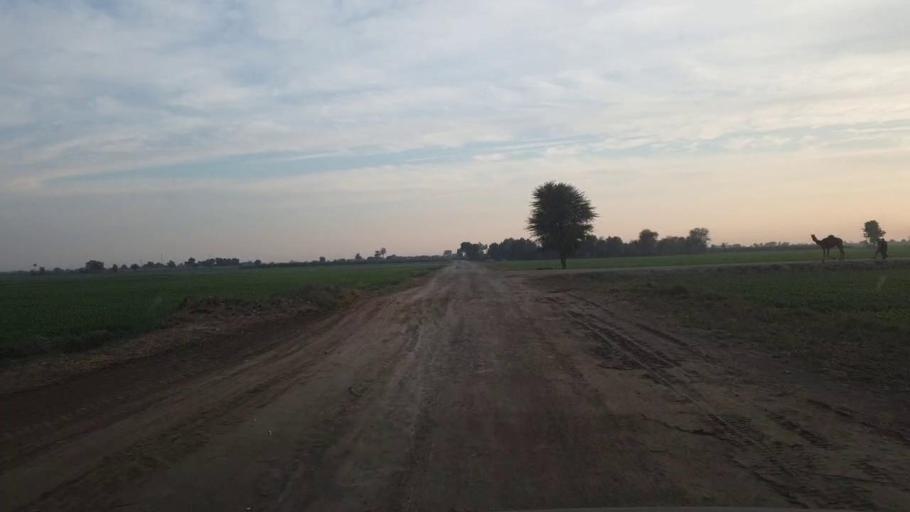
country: PK
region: Sindh
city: Shahpur Chakar
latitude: 26.0549
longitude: 68.5323
